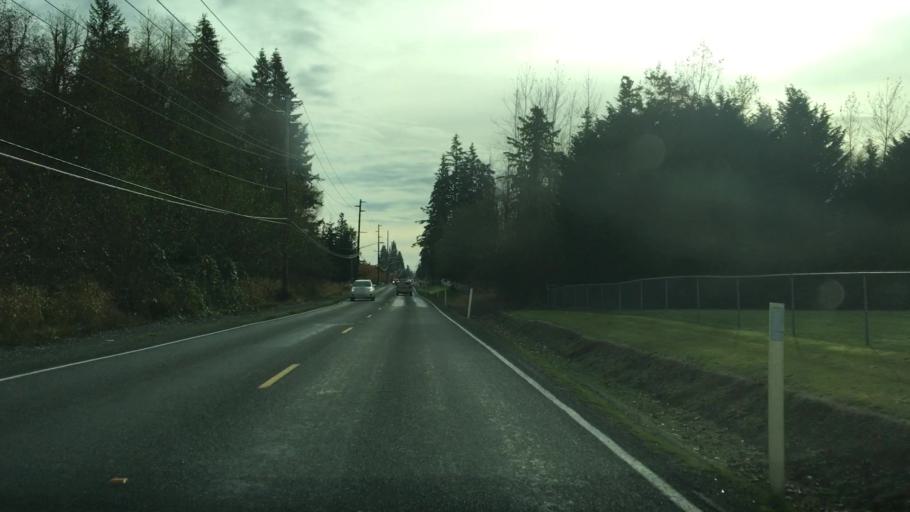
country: US
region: Washington
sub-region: Pierce County
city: South Hill
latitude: 47.1302
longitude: -122.3149
